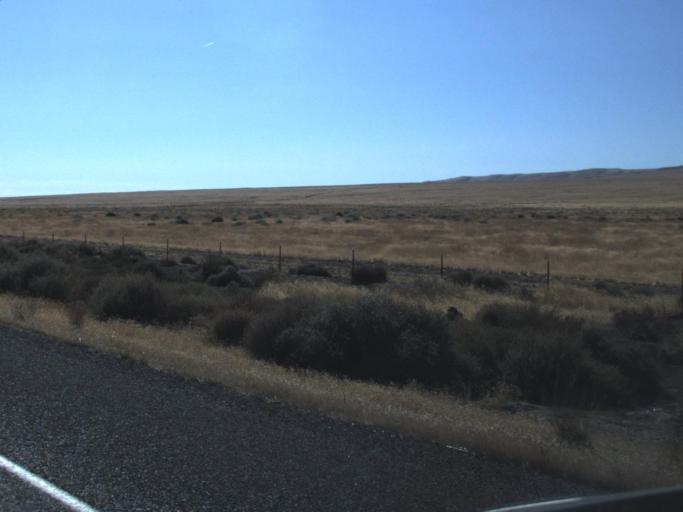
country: US
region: Washington
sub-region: Benton County
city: Benton City
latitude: 46.4724
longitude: -119.5528
